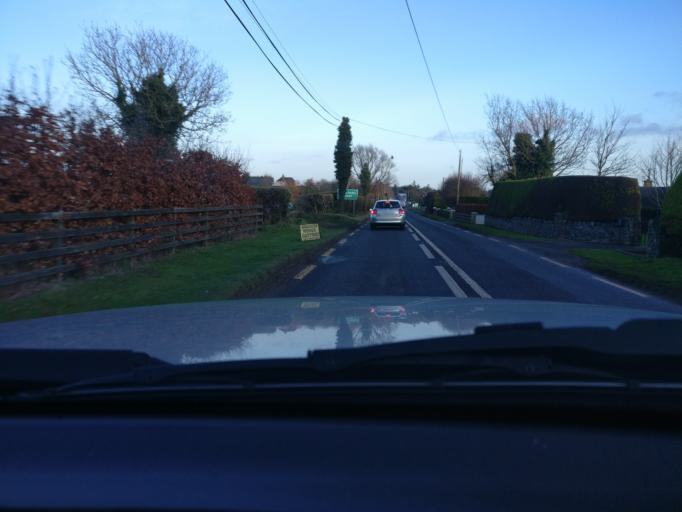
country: IE
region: Leinster
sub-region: Lu
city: Ardee
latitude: 53.8562
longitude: -6.5602
